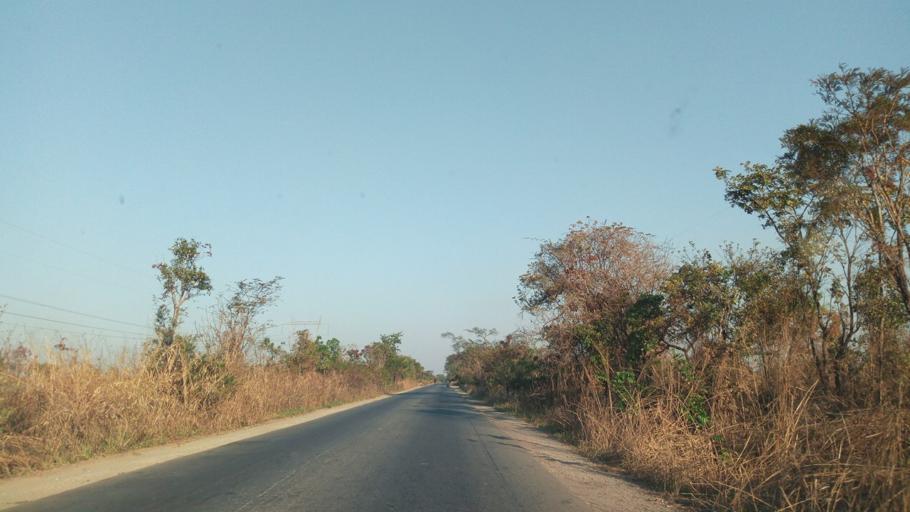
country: CD
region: Katanga
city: Likasi
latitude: -11.1197
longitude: 27.0310
